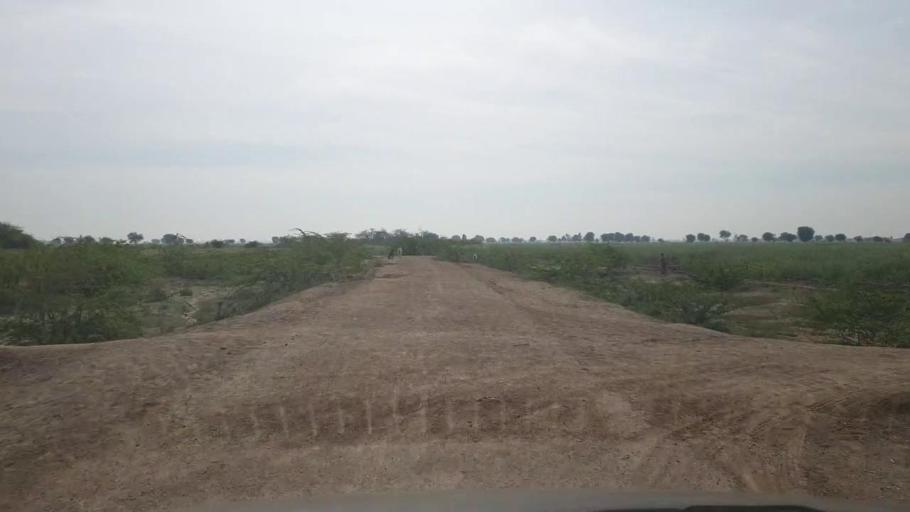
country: PK
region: Sindh
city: Umarkot
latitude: 25.3602
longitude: 69.6345
